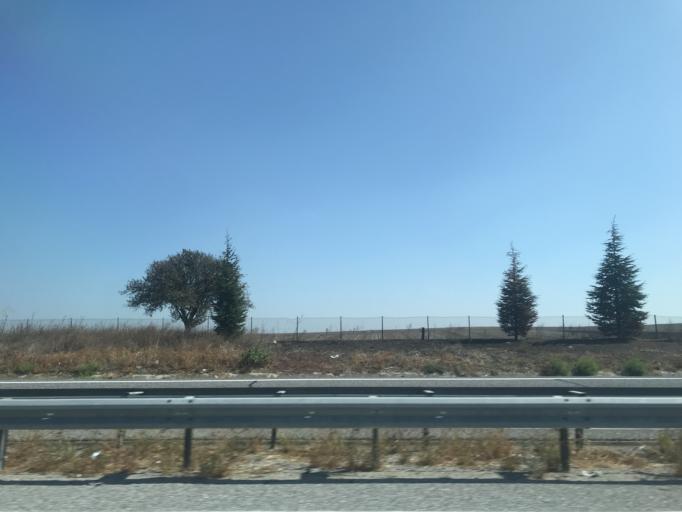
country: TR
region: Kirklareli
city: Luleburgaz
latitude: 41.3959
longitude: 27.3879
